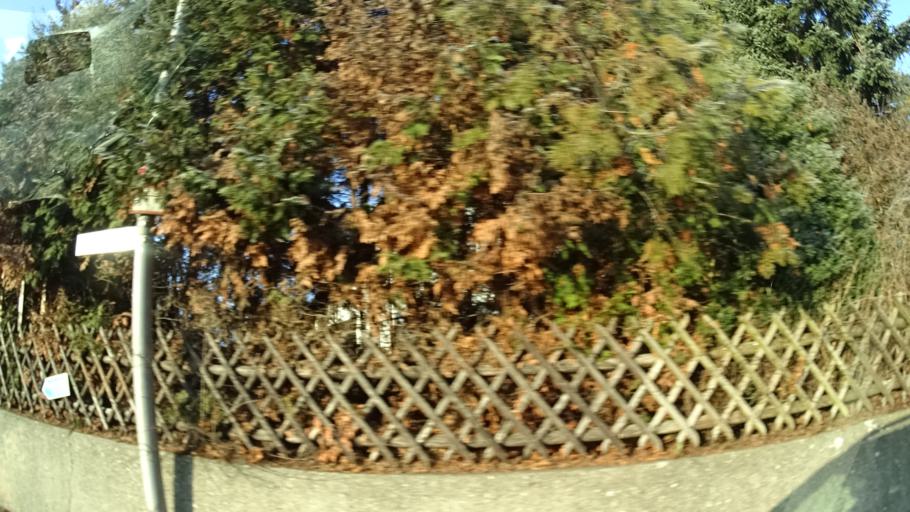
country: DE
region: Bavaria
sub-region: Upper Franconia
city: Ahorn
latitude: 50.2512
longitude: 10.9252
